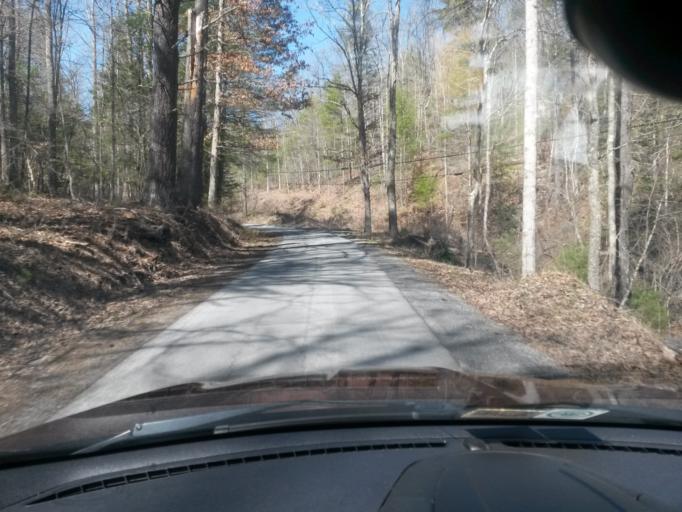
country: US
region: West Virginia
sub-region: Greenbrier County
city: White Sulphur Springs
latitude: 37.6655
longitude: -80.3171
